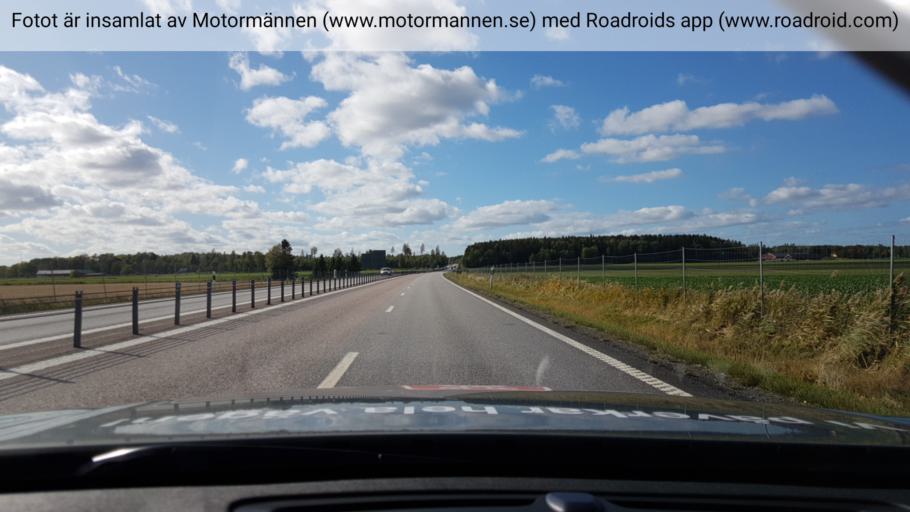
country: SE
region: Vaestmanland
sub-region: Hallstahammars Kommun
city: Hallstahammar
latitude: 59.5856
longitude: 16.1901
